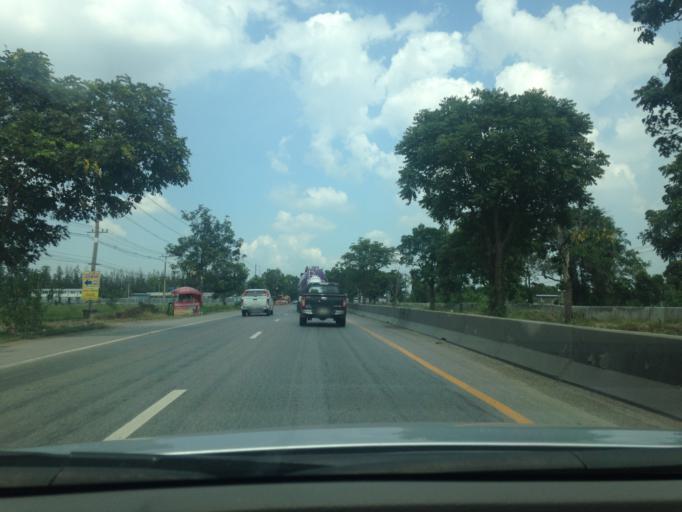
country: TH
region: Pathum Thani
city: Sam Khok
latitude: 14.0803
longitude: 100.5021
